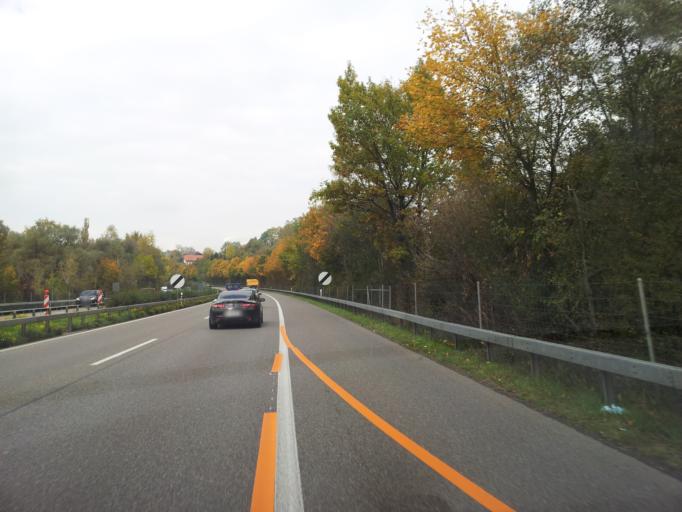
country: CH
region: Bern
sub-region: Bern-Mittelland District
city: Rubigen
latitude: 46.8984
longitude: 7.5333
